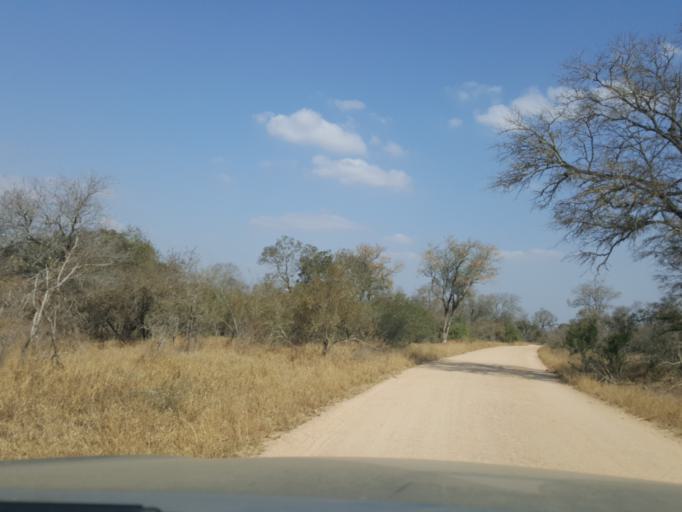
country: ZA
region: Mpumalanga
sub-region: Ehlanzeni District
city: Komatipoort
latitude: -25.2742
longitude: 31.7787
